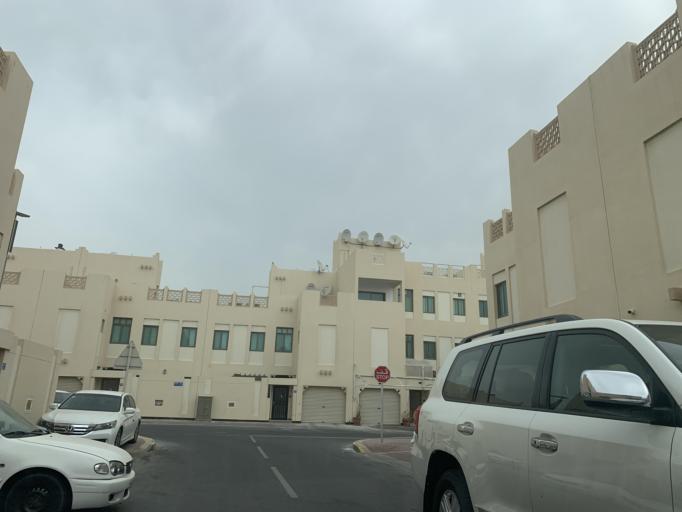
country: BH
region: Northern
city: Madinat `Isa
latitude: 26.1695
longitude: 50.5126
